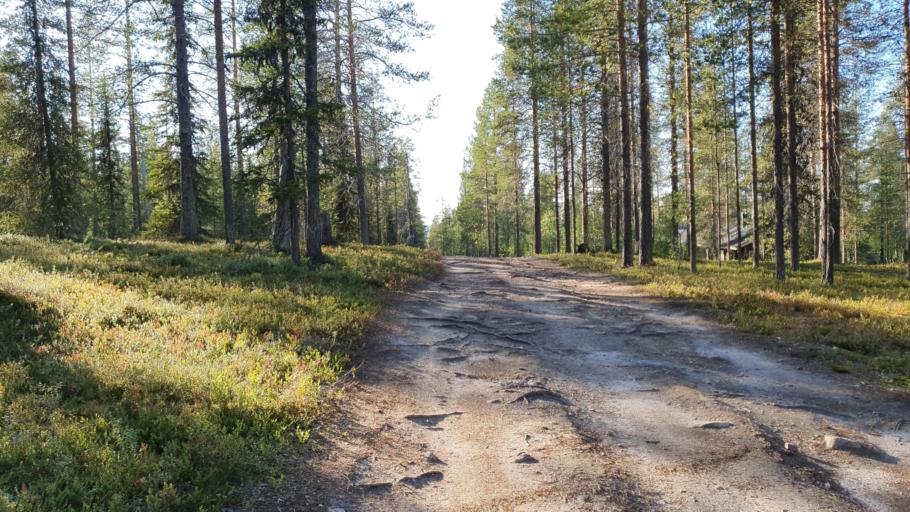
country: FI
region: Lapland
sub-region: Tunturi-Lappi
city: Kolari
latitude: 67.5989
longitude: 24.1934
